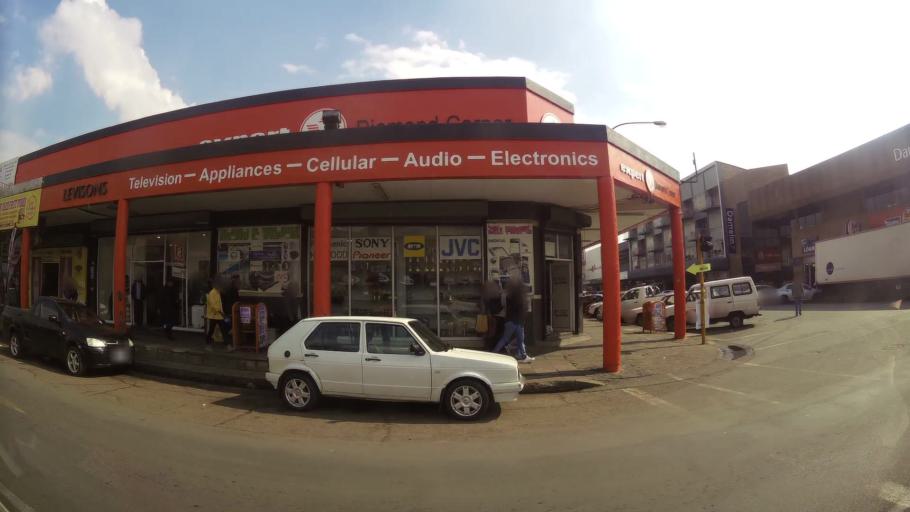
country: ZA
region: Gauteng
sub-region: Sedibeng District Municipality
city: Vereeniging
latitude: -26.6751
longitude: 27.9314
